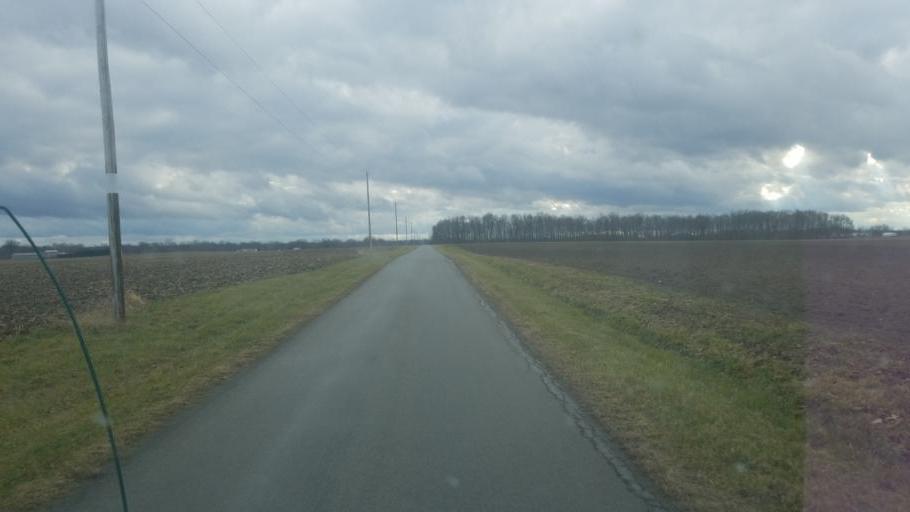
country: US
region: Ohio
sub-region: Wyandot County
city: Upper Sandusky
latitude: 40.7845
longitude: -83.1499
